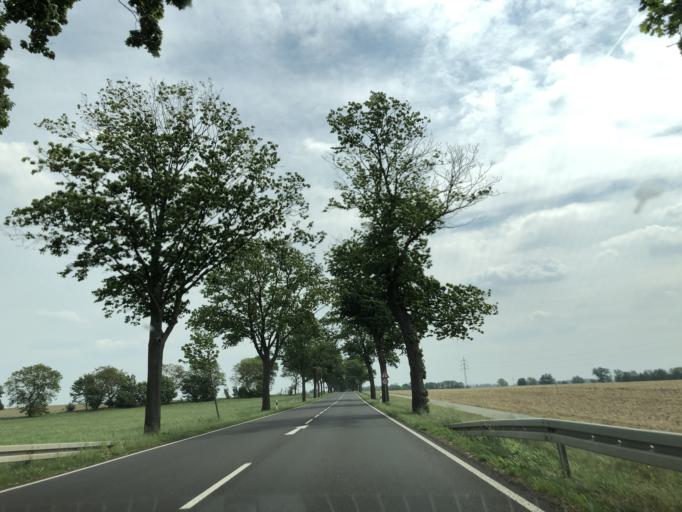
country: DE
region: Brandenburg
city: Kyritz
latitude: 52.9596
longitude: 12.3481
